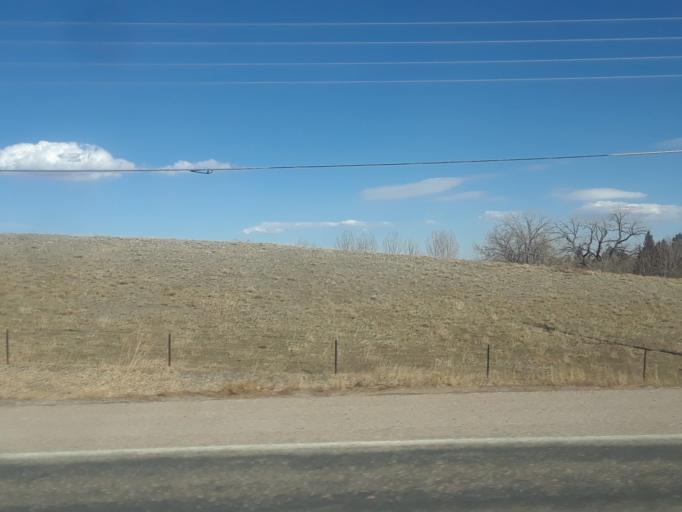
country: US
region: Colorado
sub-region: Boulder County
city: Boulder
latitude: 40.1151
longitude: -105.2823
